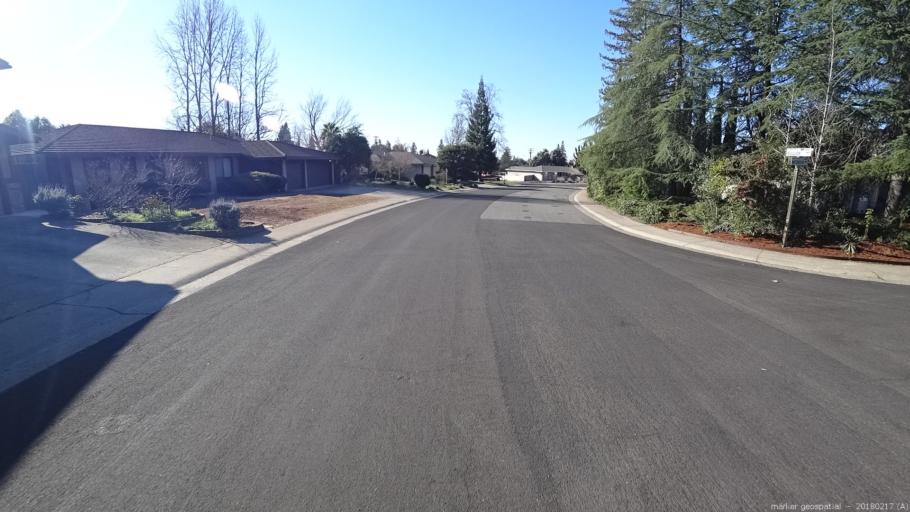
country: US
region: California
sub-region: Sacramento County
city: Folsom
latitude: 38.6613
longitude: -121.1971
